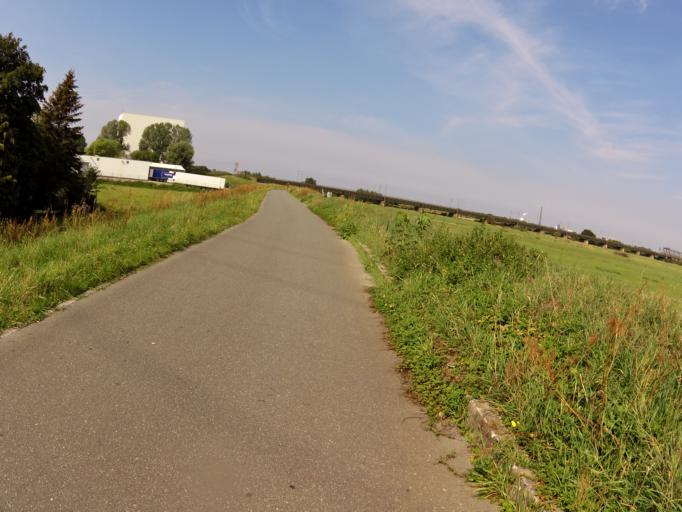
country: DE
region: Lower Saxony
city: Riede
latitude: 53.0196
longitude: 8.8789
